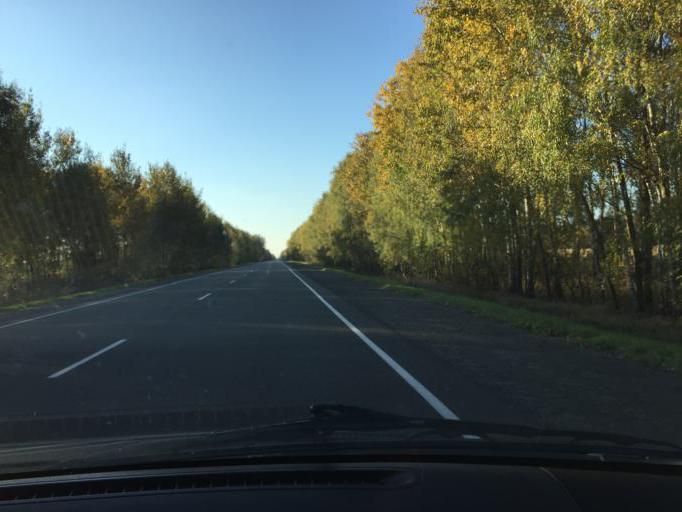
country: BY
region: Brest
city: Horad Luninyets
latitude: 52.2981
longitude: 26.7357
